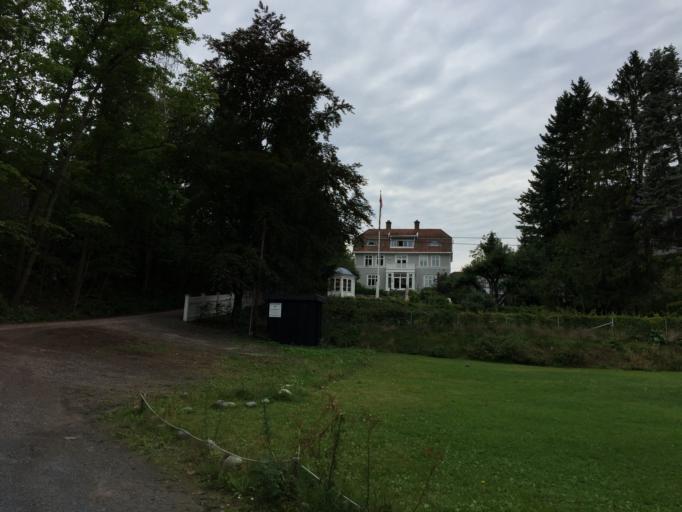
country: NO
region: Oslo
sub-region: Oslo
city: Sjolyststranda
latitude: 59.9023
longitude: 10.6893
